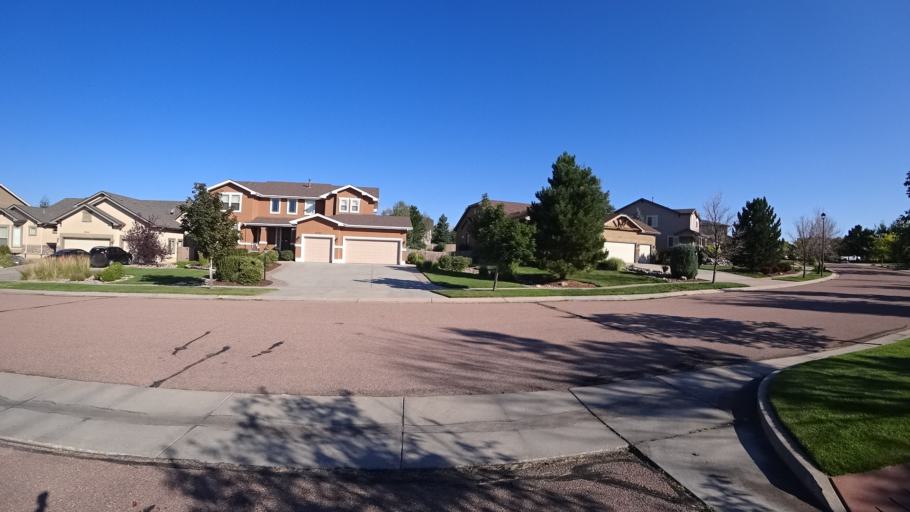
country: US
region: Colorado
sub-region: El Paso County
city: Black Forest
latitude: 38.9762
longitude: -104.7585
